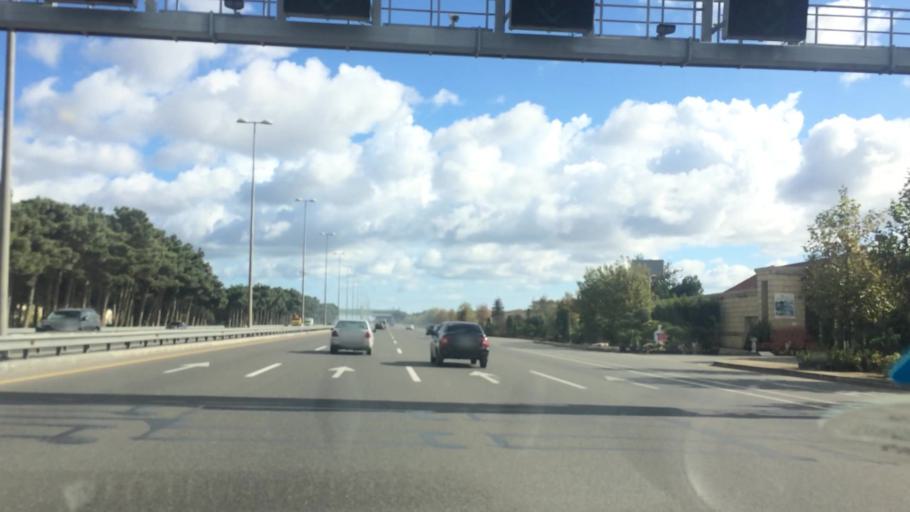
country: AZ
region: Baki
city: Biny Selo
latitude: 40.4642
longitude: 50.0860
